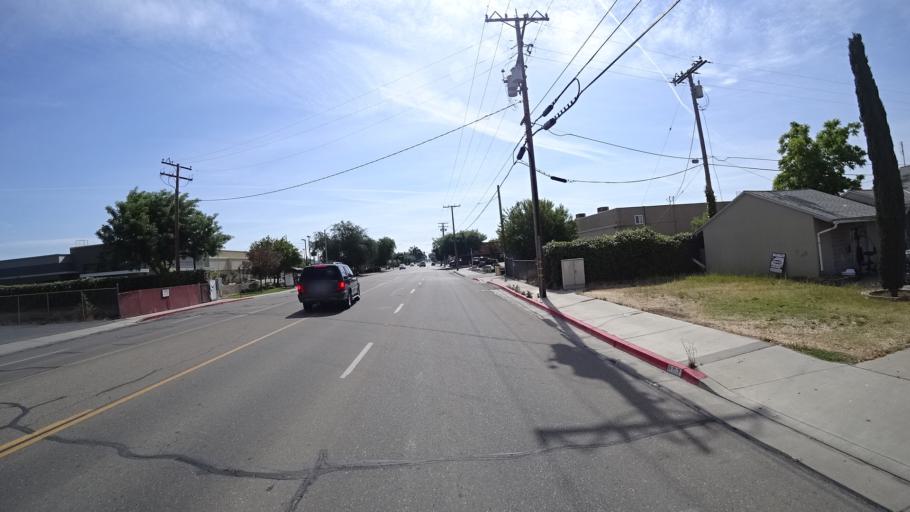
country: US
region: California
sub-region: Kings County
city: Hanford
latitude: 36.3426
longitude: -119.6570
